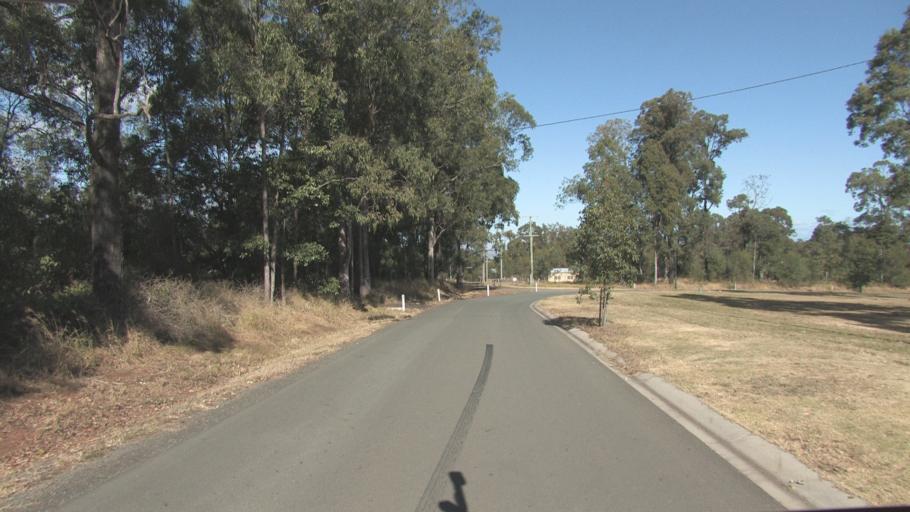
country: AU
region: Queensland
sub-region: Logan
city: Cedar Vale
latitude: -27.8949
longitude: 153.0016
